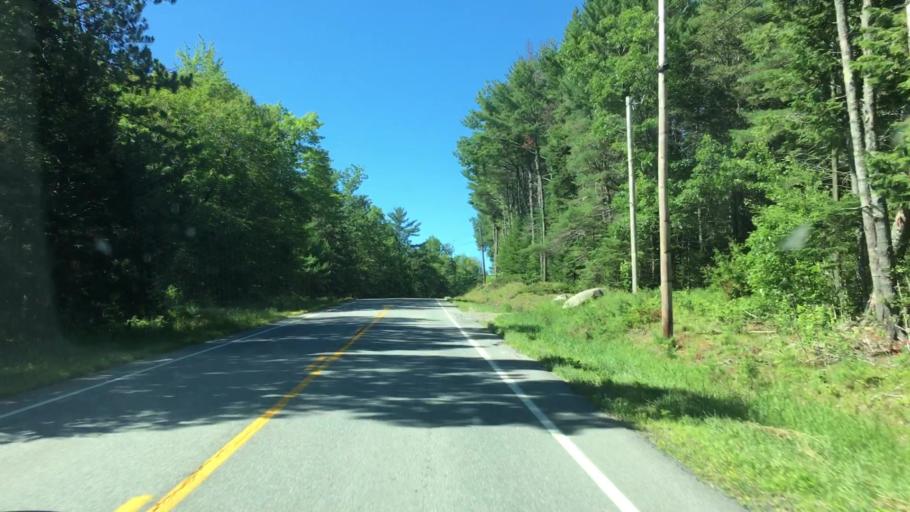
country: US
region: Maine
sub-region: Hancock County
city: Dedham
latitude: 44.6775
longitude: -68.6693
